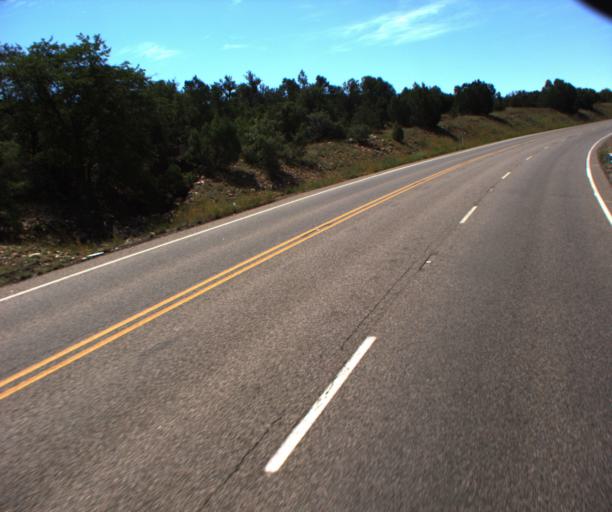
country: US
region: Arizona
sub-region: Navajo County
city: Cibecue
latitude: 33.7320
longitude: -110.5252
